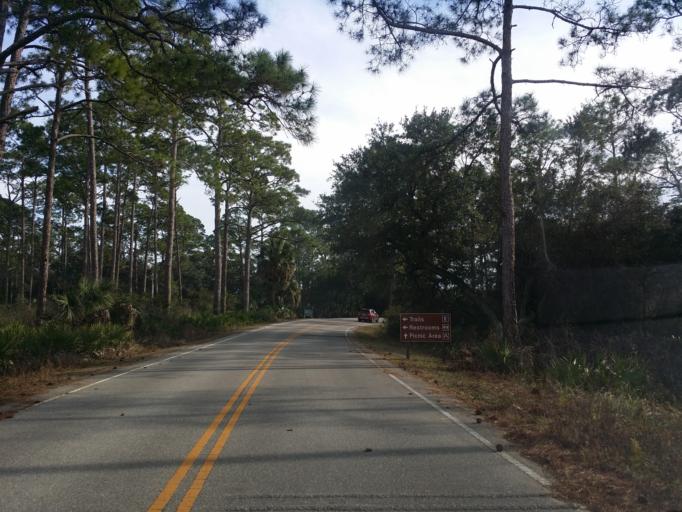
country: US
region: Florida
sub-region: Wakulla County
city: Crawfordville
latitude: 30.0889
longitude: -84.1654
